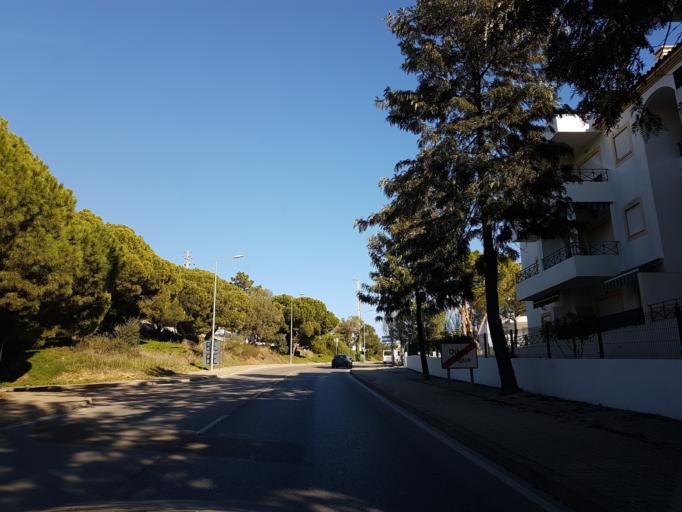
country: PT
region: Faro
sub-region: Loule
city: Boliqueime
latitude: 37.0997
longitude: -8.1854
